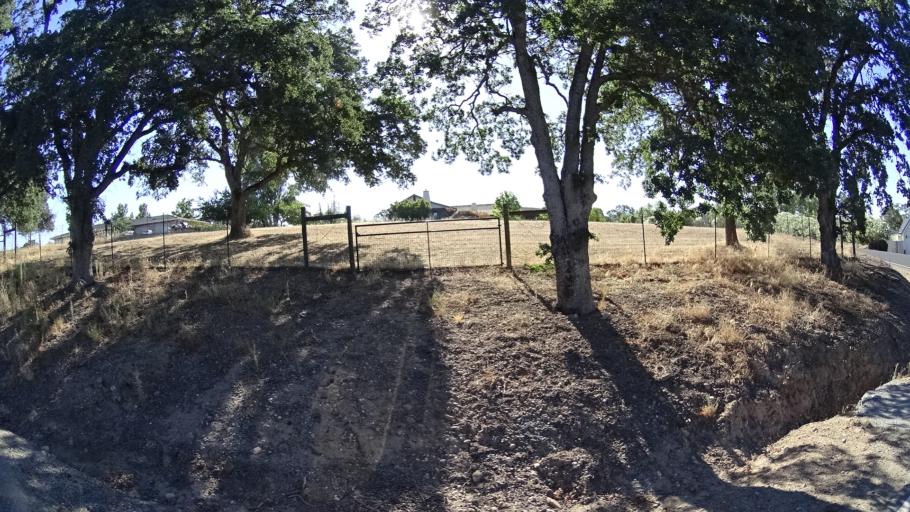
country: US
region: California
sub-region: Calaveras County
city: Rancho Calaveras
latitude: 38.1193
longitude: -120.8679
